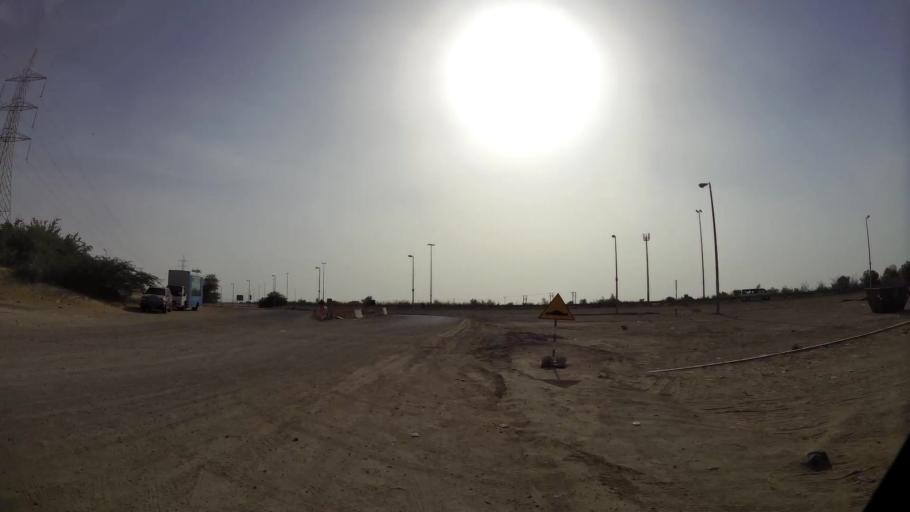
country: AE
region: Abu Dhabi
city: Al Ain
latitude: 24.0606
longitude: 55.7271
